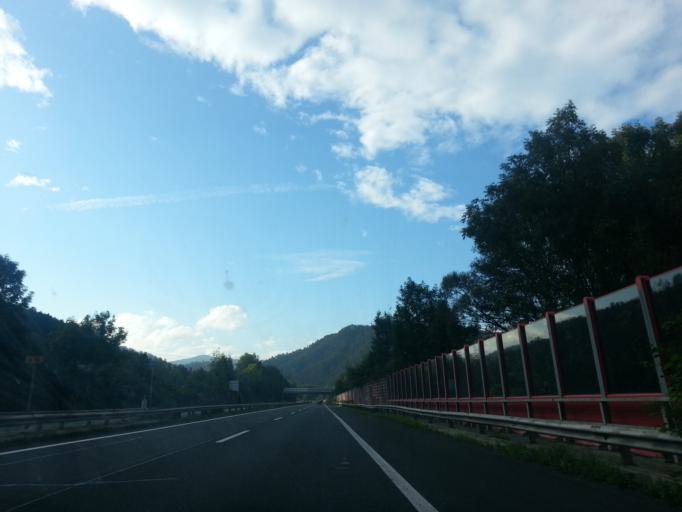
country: AT
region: Styria
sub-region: Politischer Bezirk Graz-Umgebung
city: Deutschfeistritz
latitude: 47.2108
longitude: 15.3094
